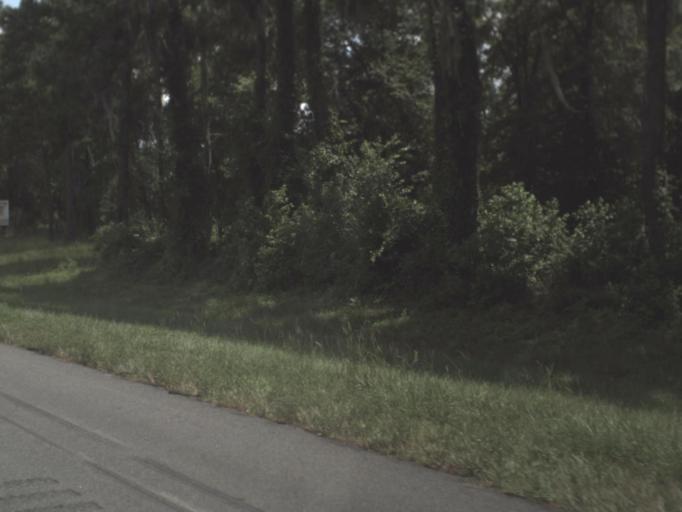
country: US
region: Florida
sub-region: Hamilton County
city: Jasper
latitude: 30.4314
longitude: -82.9104
